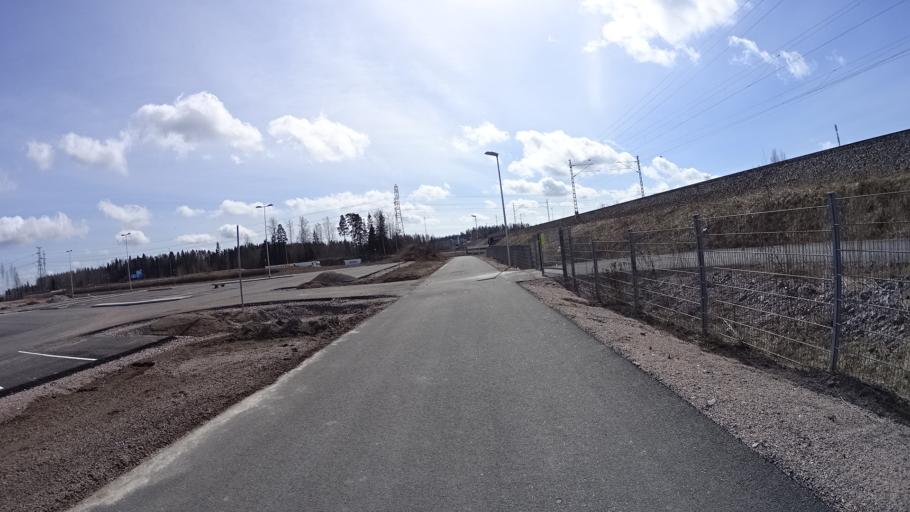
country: FI
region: Uusimaa
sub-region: Helsinki
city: Kilo
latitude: 60.2932
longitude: 24.8451
